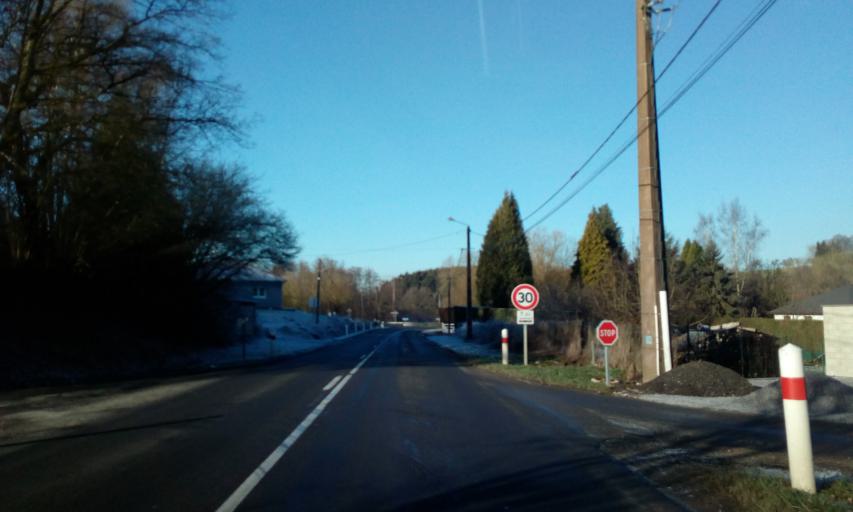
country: FR
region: Champagne-Ardenne
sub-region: Departement des Ardennes
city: Rimogne
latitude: 49.8287
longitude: 4.5010
